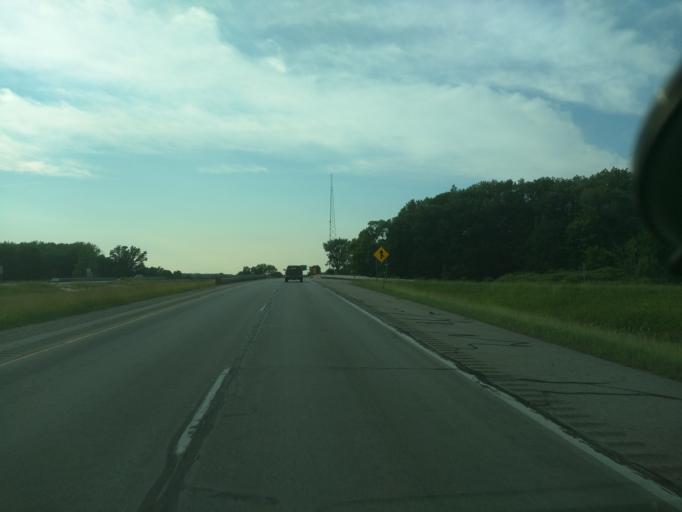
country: US
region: Michigan
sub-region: Ingham County
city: Holt
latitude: 42.6735
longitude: -84.4944
